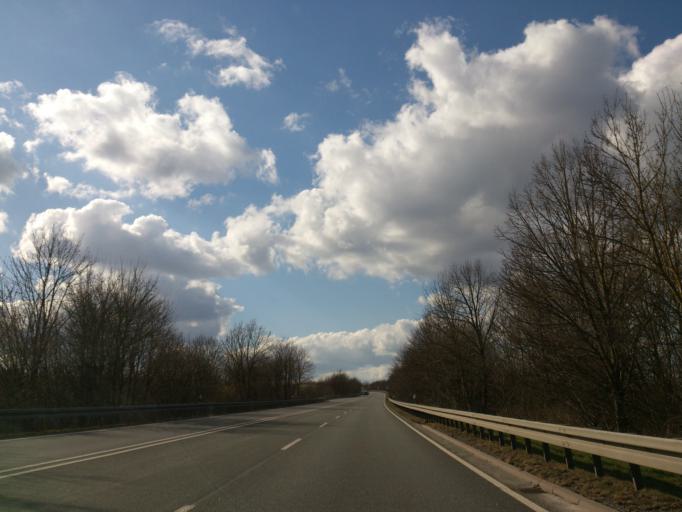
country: DE
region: North Rhine-Westphalia
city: Brakel
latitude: 51.7006
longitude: 9.2093
